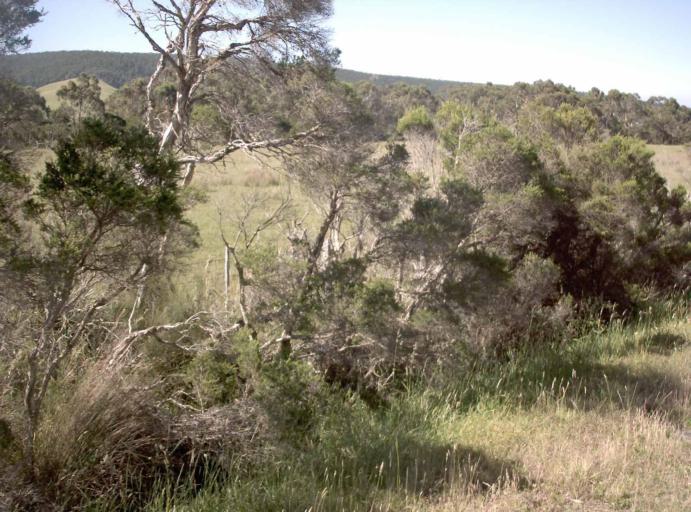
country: AU
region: Victoria
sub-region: Latrobe
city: Morwell
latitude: -38.6386
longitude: 146.5216
